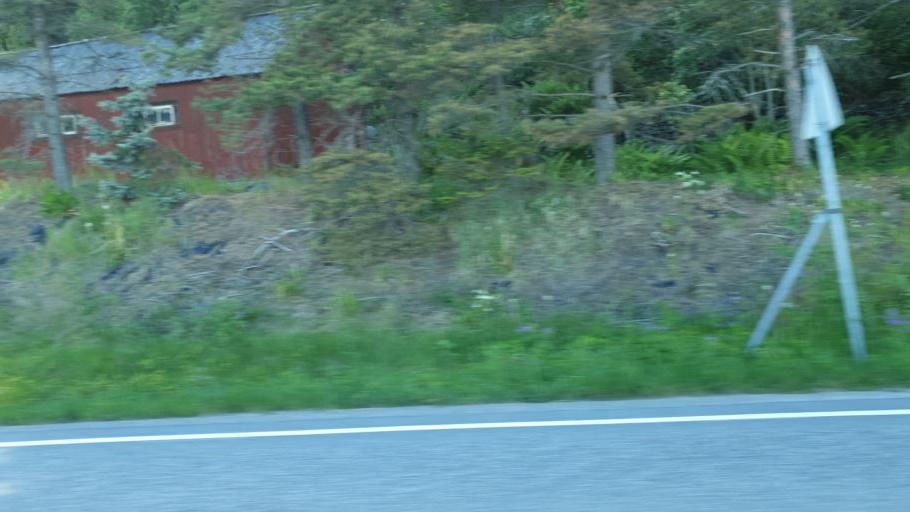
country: NO
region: Sor-Trondelag
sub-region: Skaun
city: Borsa
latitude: 63.5042
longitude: 10.1297
